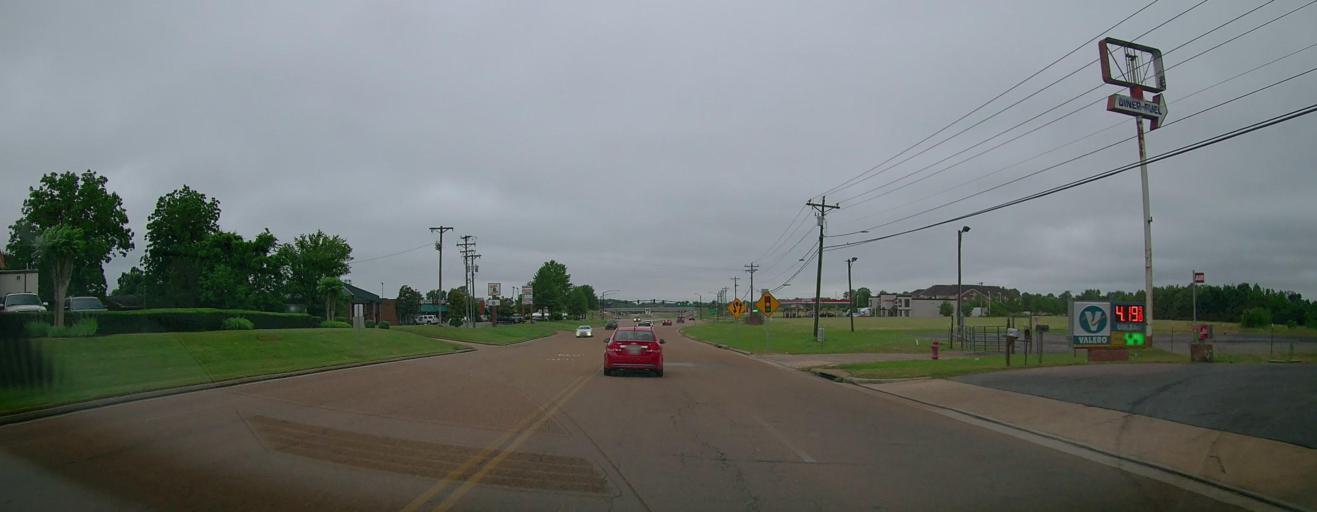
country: US
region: Mississippi
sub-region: De Soto County
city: Olive Branch
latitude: 34.9321
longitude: -89.7949
